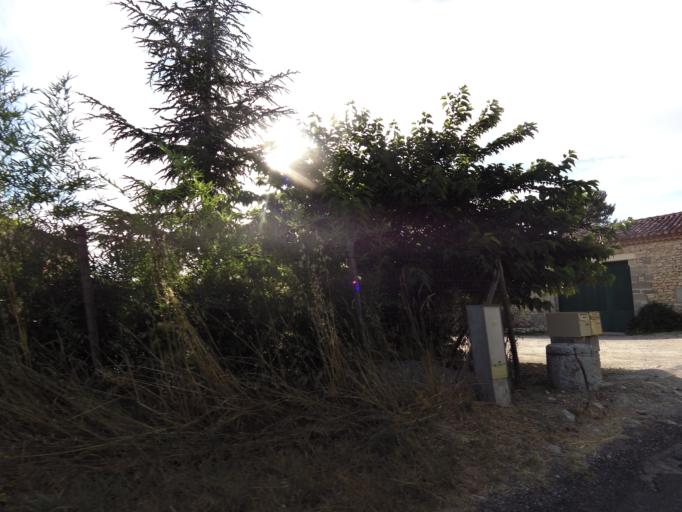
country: FR
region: Languedoc-Roussillon
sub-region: Departement du Gard
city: Congenies
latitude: 43.8184
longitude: 4.1476
